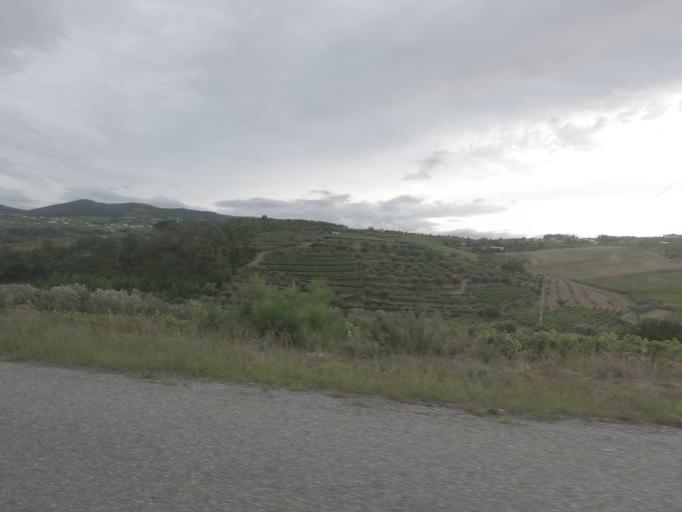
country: PT
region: Vila Real
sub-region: Sabrosa
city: Sabrosa
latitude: 41.2645
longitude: -7.5661
